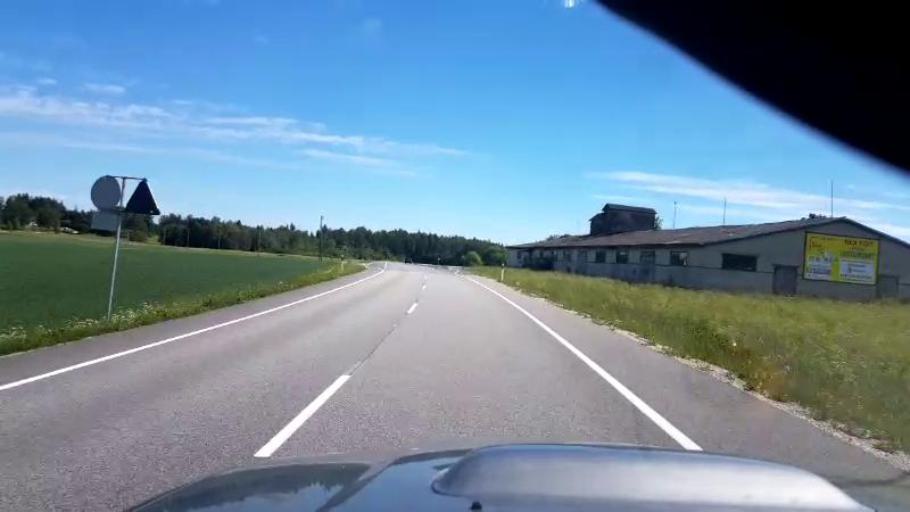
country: EE
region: Jaervamaa
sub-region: Jaerva-Jaani vald
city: Jarva-Jaani
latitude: 59.0021
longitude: 25.9335
